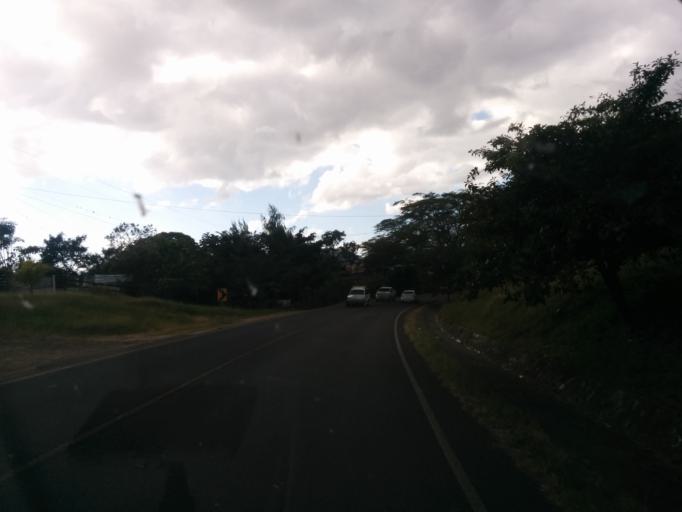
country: NI
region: Esteli
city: Esteli
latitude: 13.0607
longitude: -86.3435
